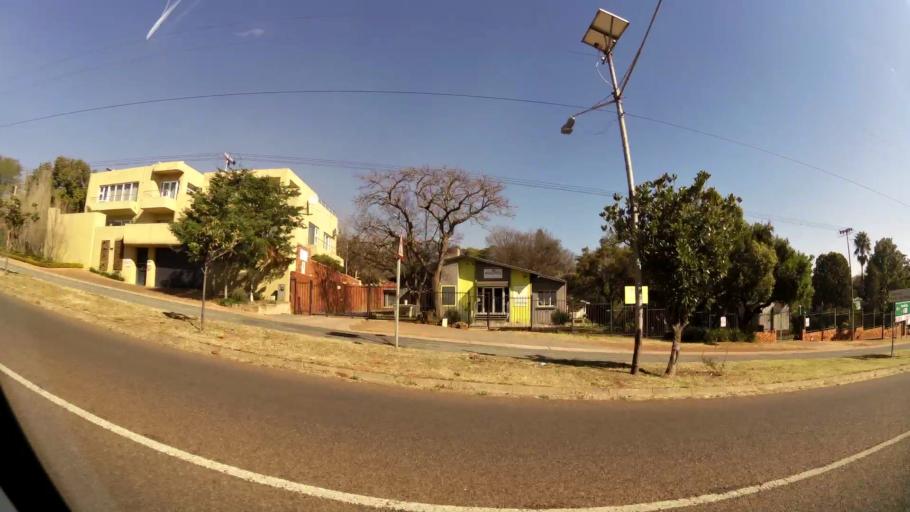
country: ZA
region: Gauteng
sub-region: City of Tshwane Metropolitan Municipality
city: Pretoria
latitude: -25.7767
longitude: 28.2259
